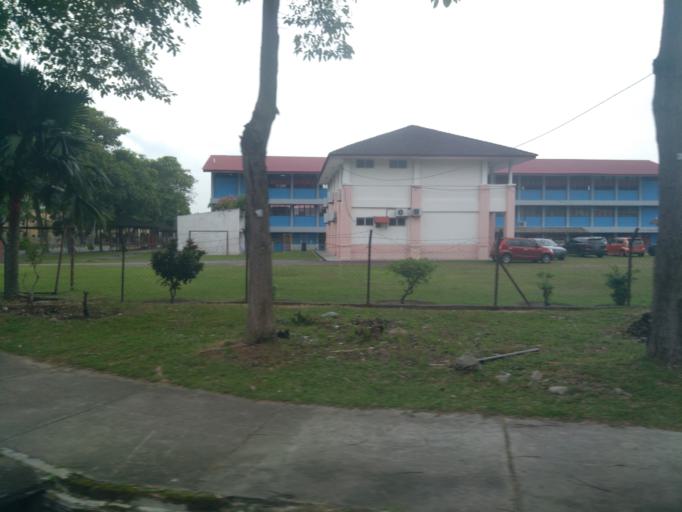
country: MY
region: Johor
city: Johor Bahru
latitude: 1.4939
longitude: 103.7048
